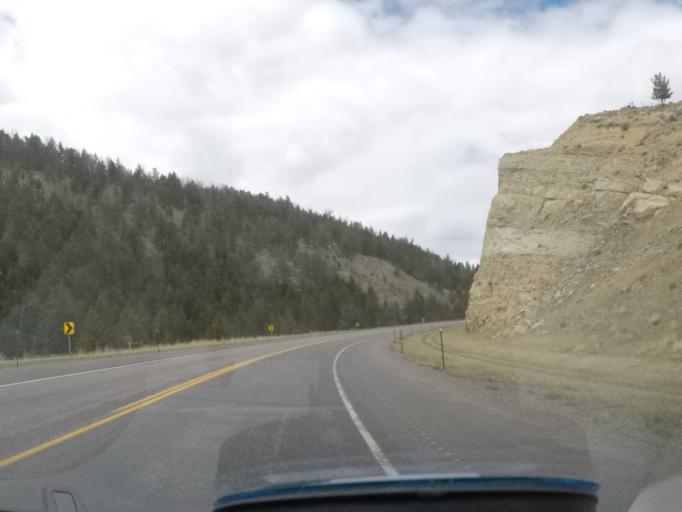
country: US
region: Wyoming
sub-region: Sublette County
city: Pinedale
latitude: 43.5788
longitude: -109.7601
